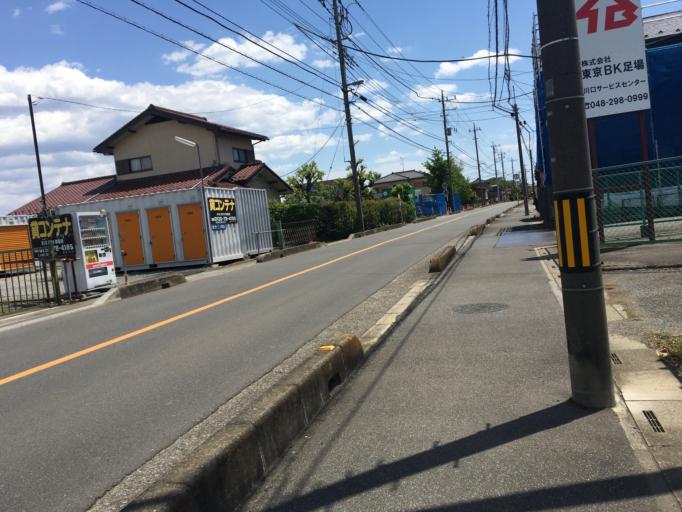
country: JP
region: Saitama
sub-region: Kawaguchi-shi
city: Hatogaya-honcho
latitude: 35.8470
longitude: 139.7524
